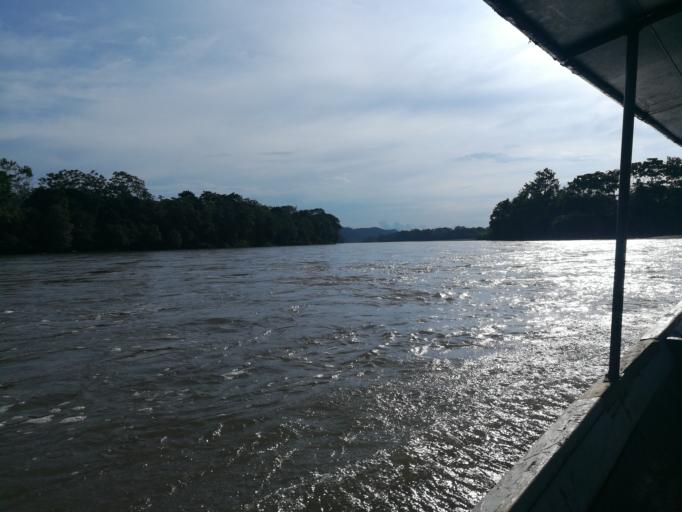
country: EC
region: Orellana
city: Boca Suno
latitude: -0.8517
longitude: -77.2378
